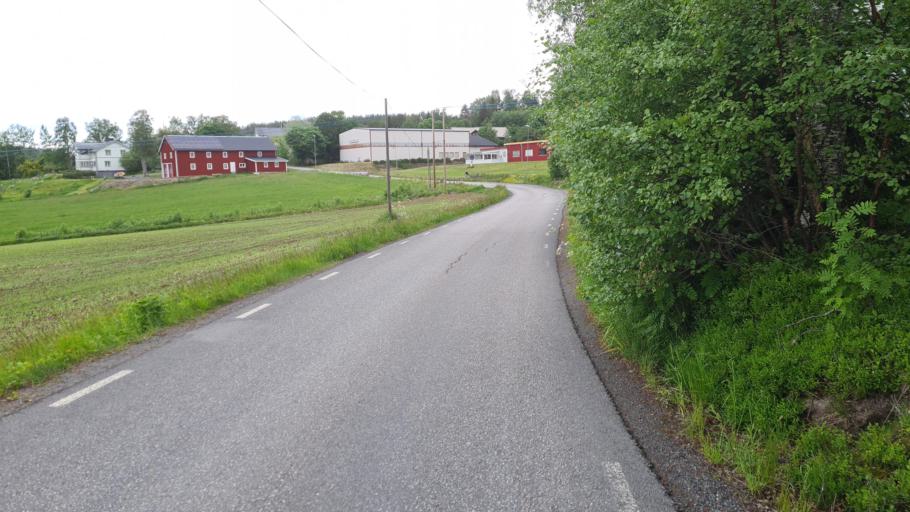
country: SE
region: Vaesternorrland
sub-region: Kramfors Kommun
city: Nordingra
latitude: 62.9812
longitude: 18.4313
